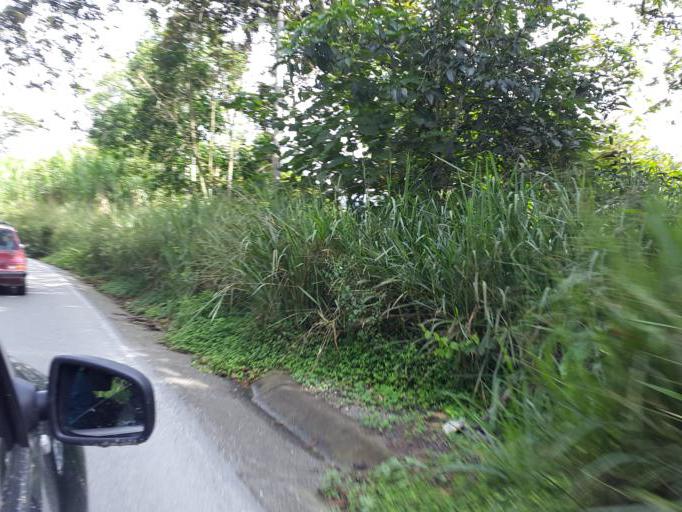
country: CO
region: Quindio
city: Cordoba
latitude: 4.4062
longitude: -75.7282
